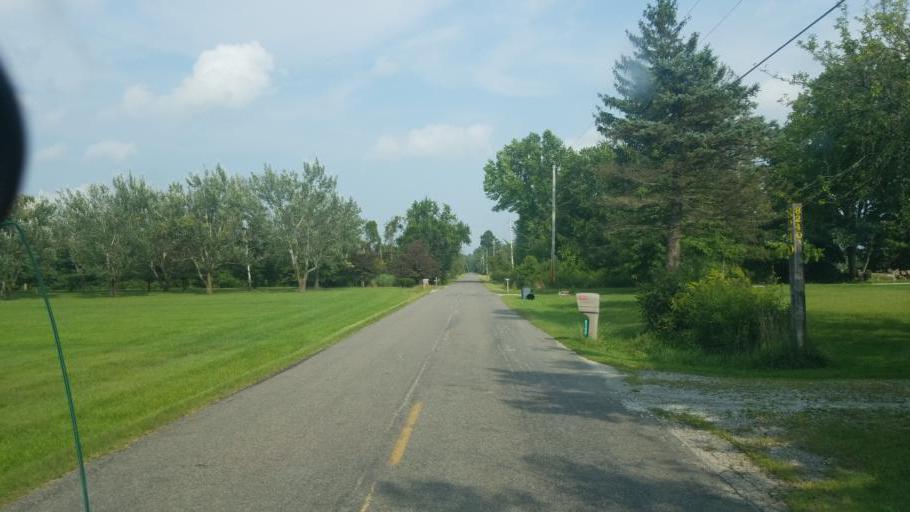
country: US
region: Ohio
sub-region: Medina County
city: Medina
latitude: 41.1578
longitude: -81.9861
